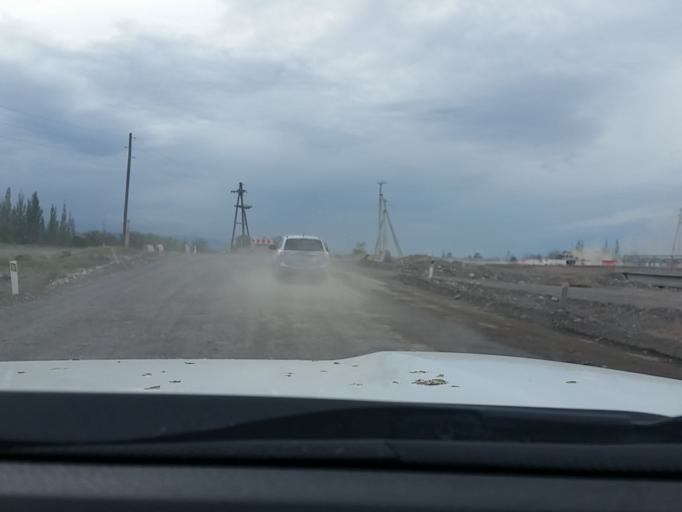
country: KZ
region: Almaty Oblysy
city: Turgen'
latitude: 43.6007
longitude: 78.3019
